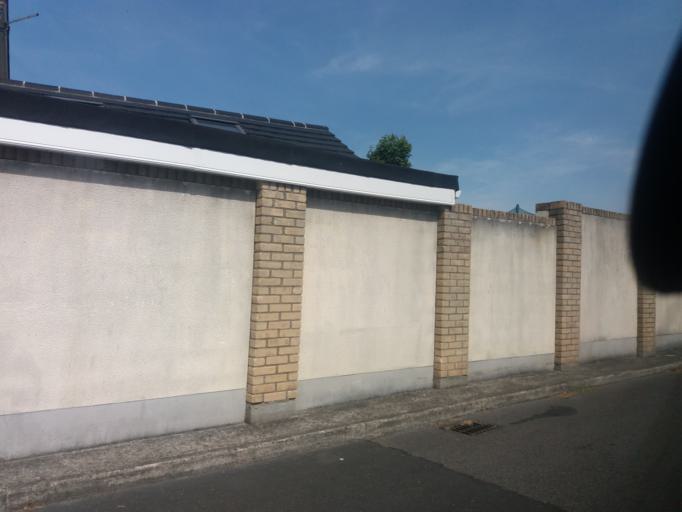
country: IE
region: Leinster
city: Lusk
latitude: 53.5240
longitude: -6.1707
